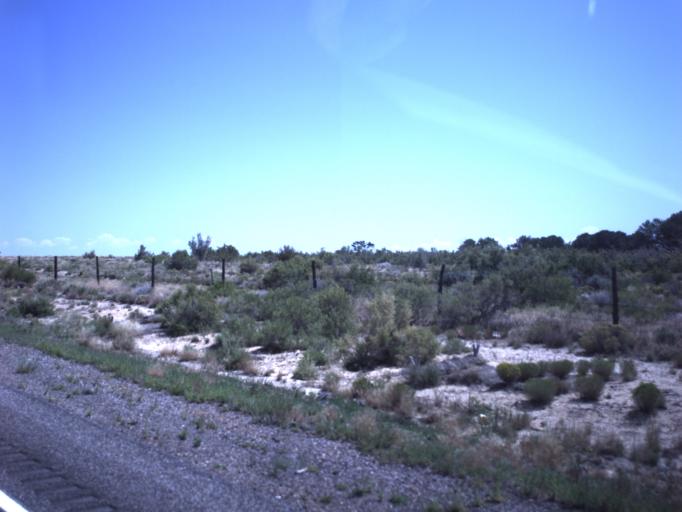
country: US
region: Utah
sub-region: Emery County
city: Ferron
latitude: 38.8943
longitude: -111.2788
